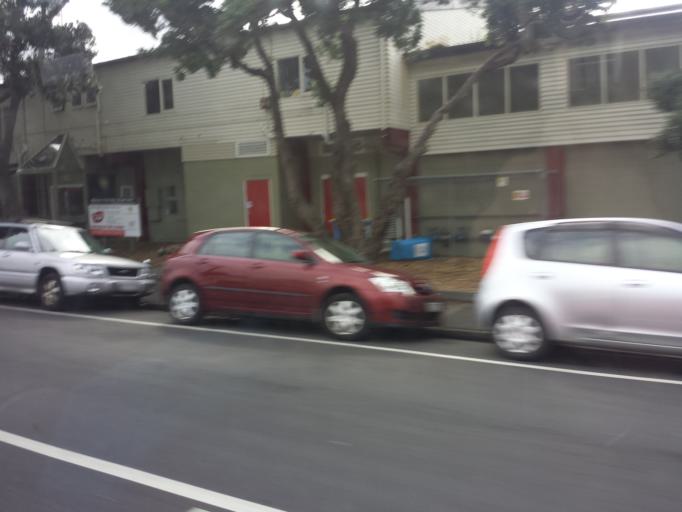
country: NZ
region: Wellington
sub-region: Wellington City
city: Wellington
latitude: -41.3145
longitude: 174.7928
